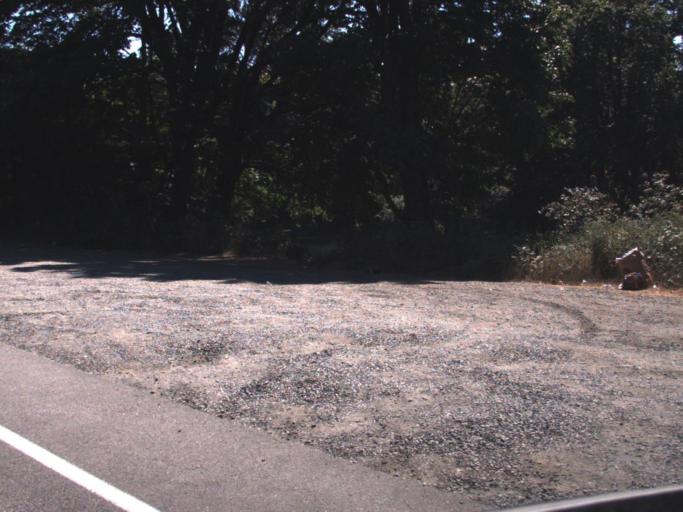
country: US
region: Washington
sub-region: King County
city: Fall City
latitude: 47.5685
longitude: -121.8800
